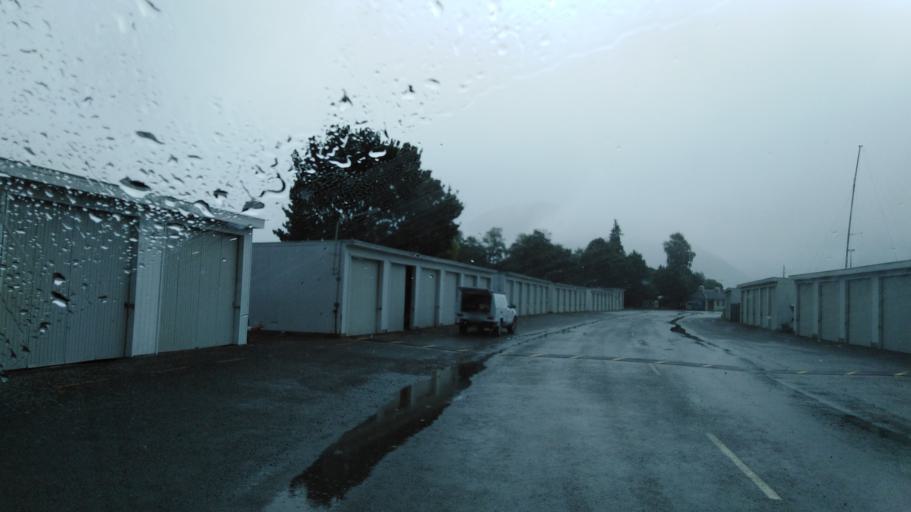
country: NZ
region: Marlborough
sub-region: Marlborough District
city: Picton
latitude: -41.2776
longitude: 173.7688
